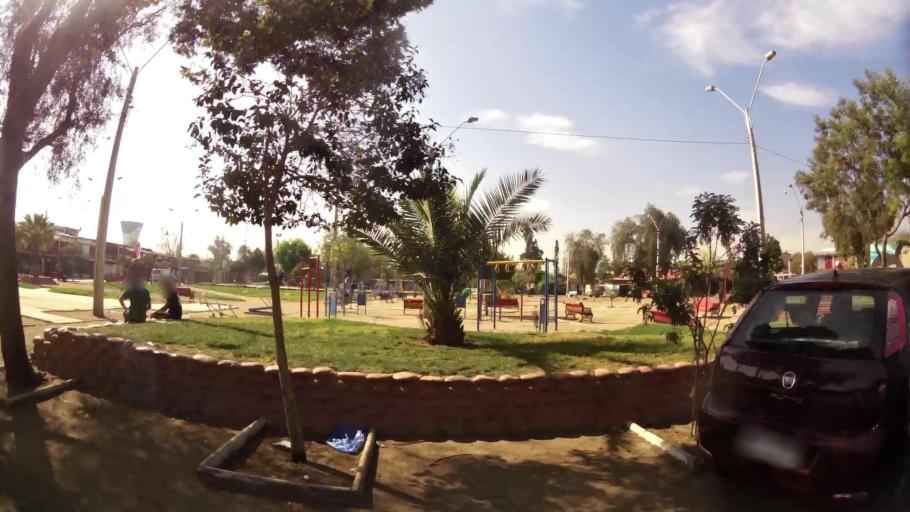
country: CL
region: Santiago Metropolitan
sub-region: Provincia de Santiago
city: Lo Prado
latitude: -33.4431
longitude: -70.7619
